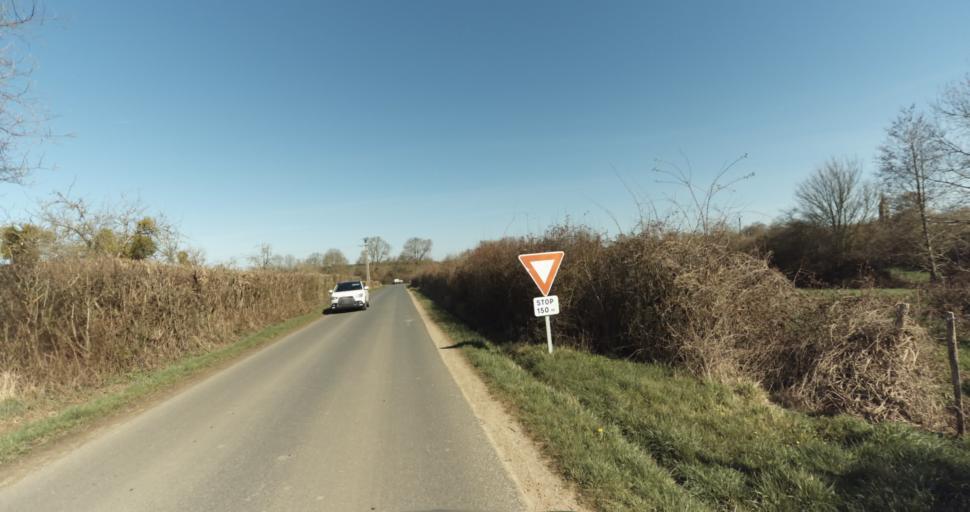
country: FR
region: Lower Normandy
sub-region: Departement de l'Orne
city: Trun
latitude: 48.9383
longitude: 0.0292
